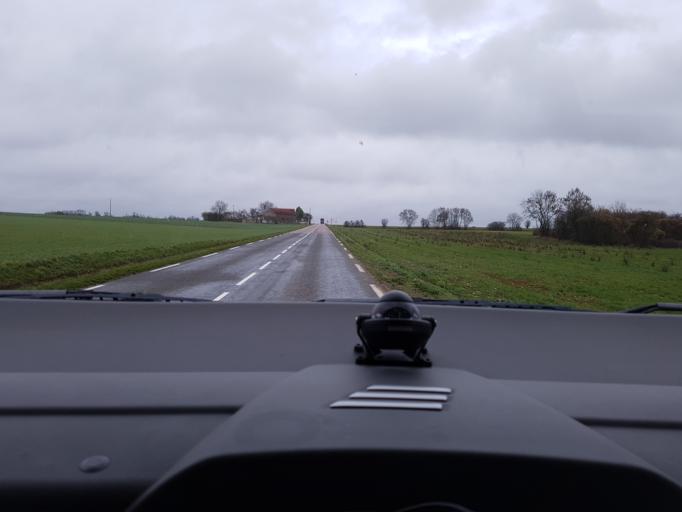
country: FR
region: Picardie
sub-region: Departement de l'Oise
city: Songeons
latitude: 49.5122
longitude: 1.8151
